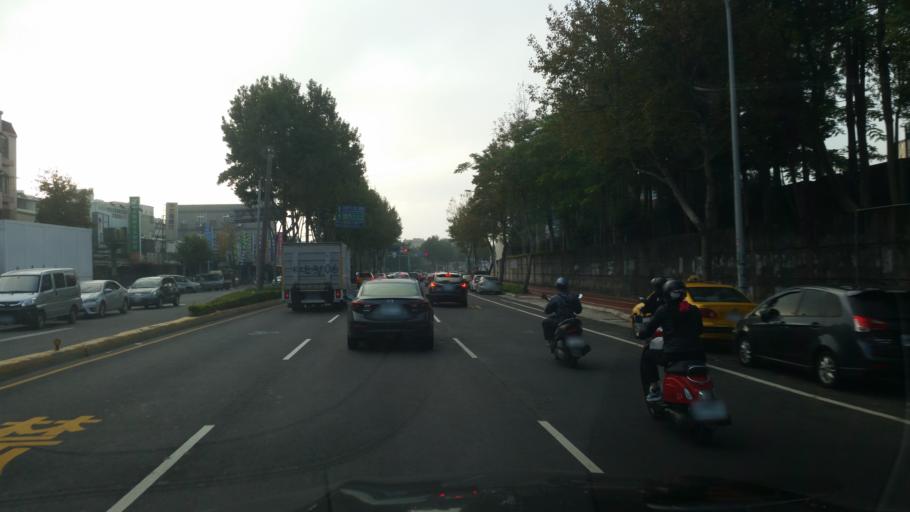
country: TW
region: Taiwan
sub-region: Taoyuan
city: Taoyuan
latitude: 25.0530
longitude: 121.3587
